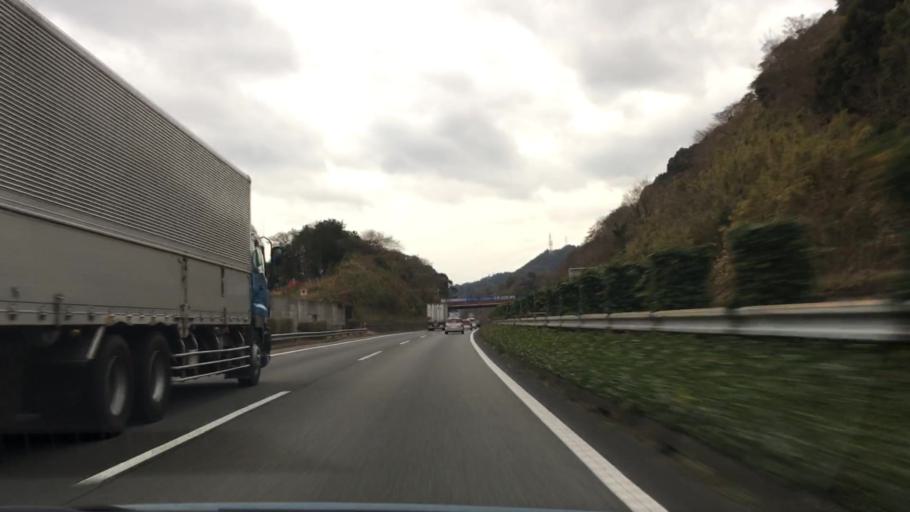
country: JP
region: Shizuoka
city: Fujinomiya
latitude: 35.1521
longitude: 138.6167
